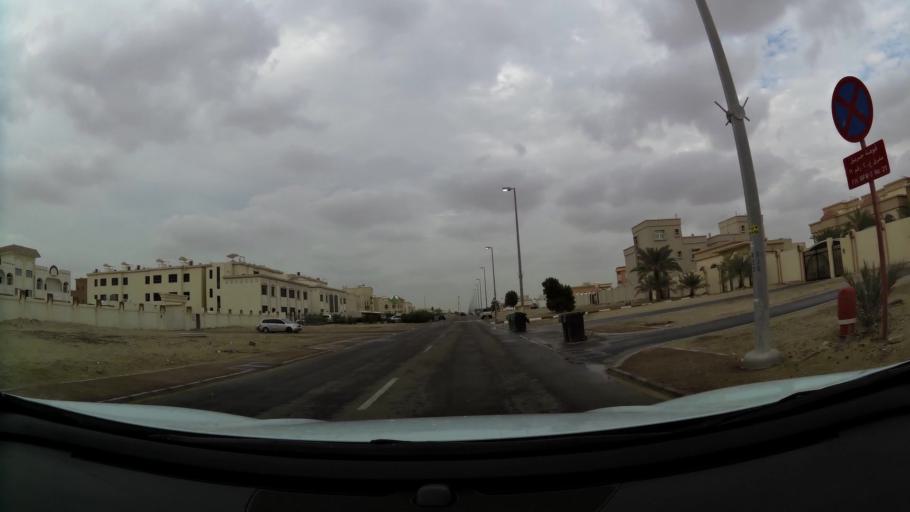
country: AE
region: Abu Dhabi
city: Abu Dhabi
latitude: 24.3498
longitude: 54.6297
